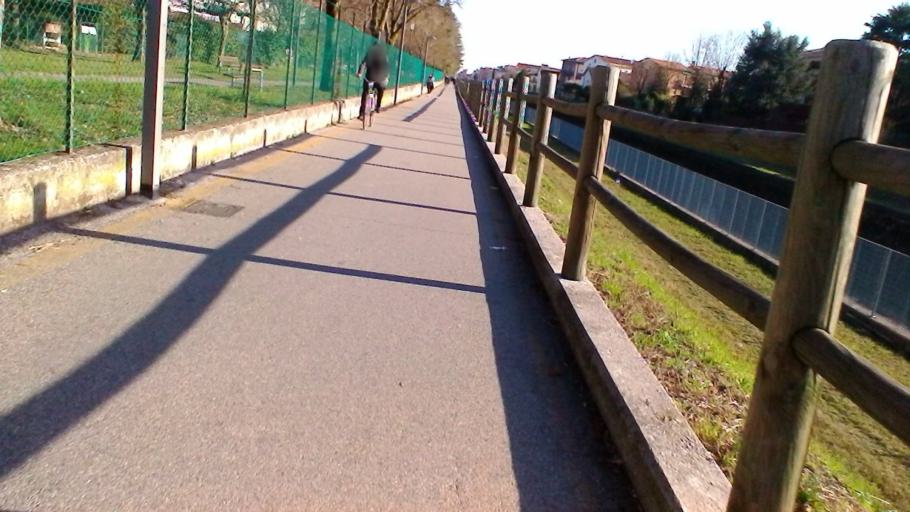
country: IT
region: Veneto
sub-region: Provincia di Verona
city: Parona
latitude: 45.4532
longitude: 10.9608
